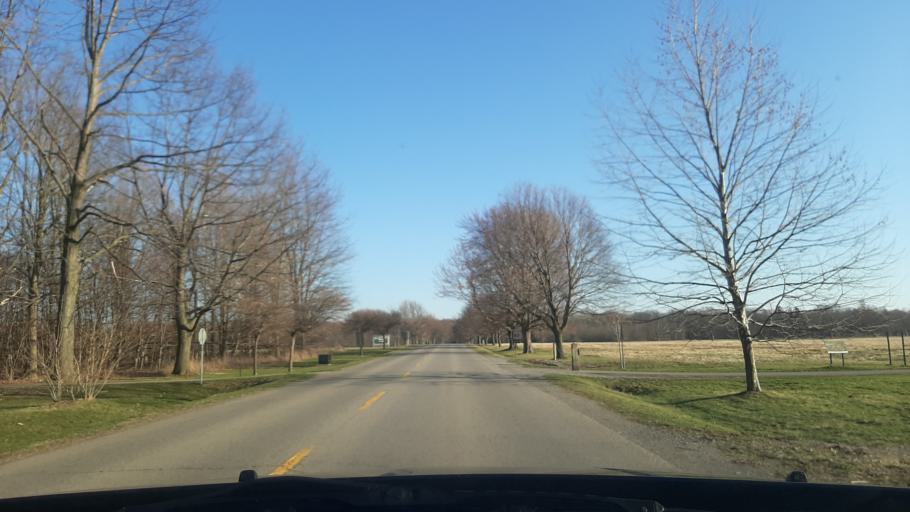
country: US
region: New York
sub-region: Niagara County
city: Youngstown
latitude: 43.2507
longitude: -79.0656
